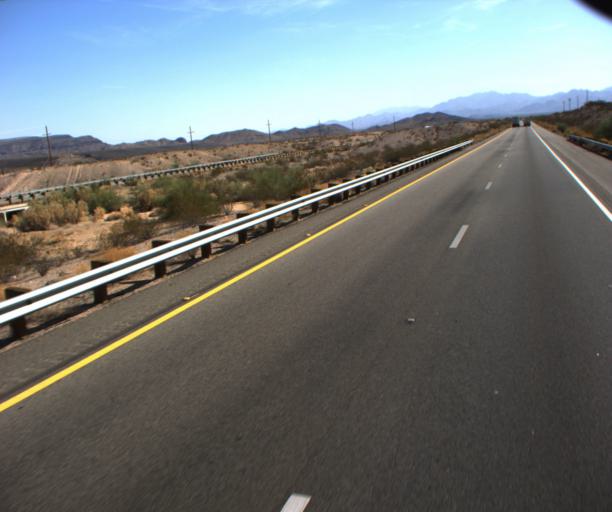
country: US
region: Arizona
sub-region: Mohave County
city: Desert Hills
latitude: 34.7706
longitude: -114.1940
